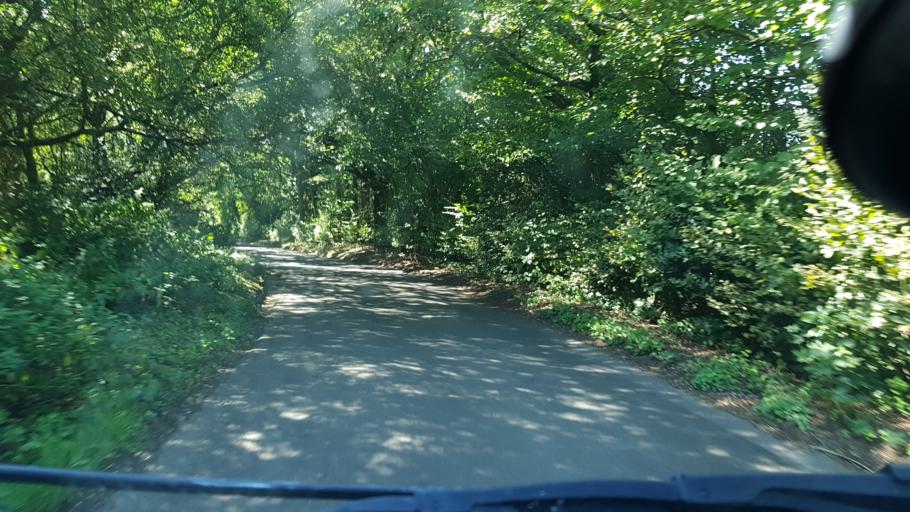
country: GB
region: England
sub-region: Surrey
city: Cranleigh
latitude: 51.1649
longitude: -0.4951
